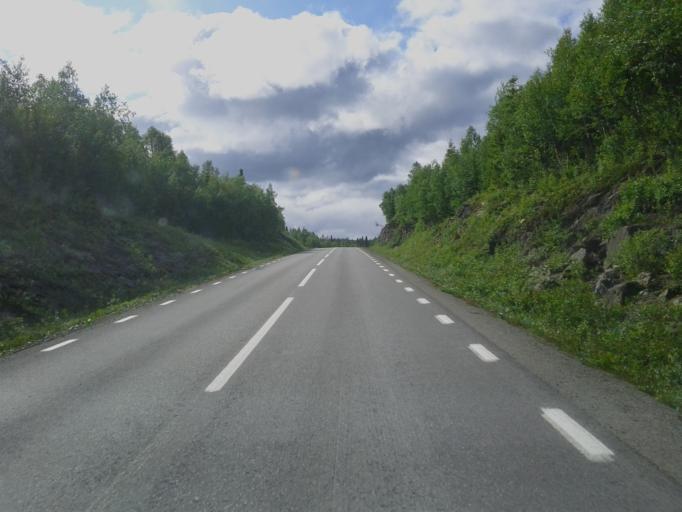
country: NO
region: Nordland
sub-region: Rana
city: Mo i Rana
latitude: 65.7119
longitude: 15.2264
